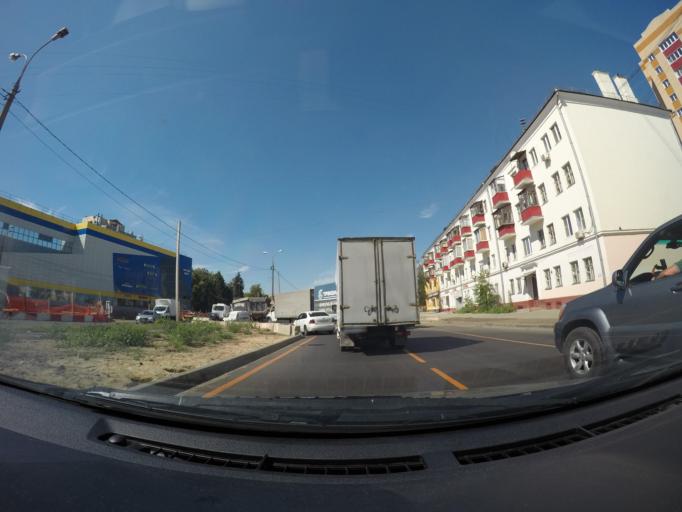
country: RU
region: Moskovskaya
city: Lyubertsy
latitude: 55.6801
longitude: 37.8908
